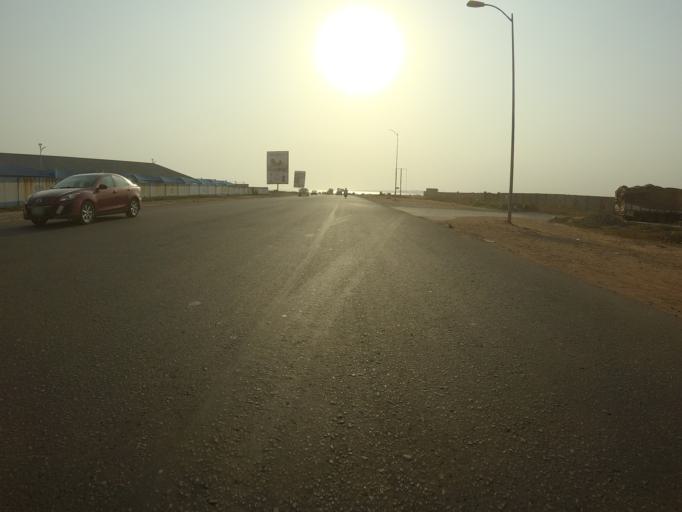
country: GH
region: Greater Accra
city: Nungua
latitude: 5.6152
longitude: -0.0266
